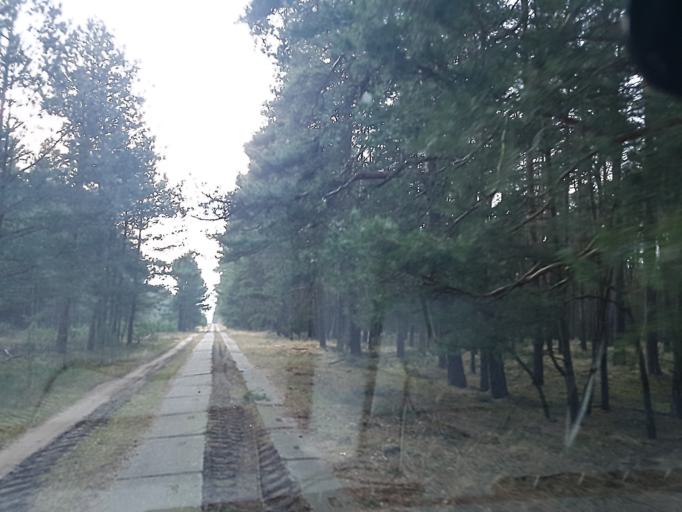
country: DE
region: Brandenburg
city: Wollin
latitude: 52.2564
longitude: 12.5117
